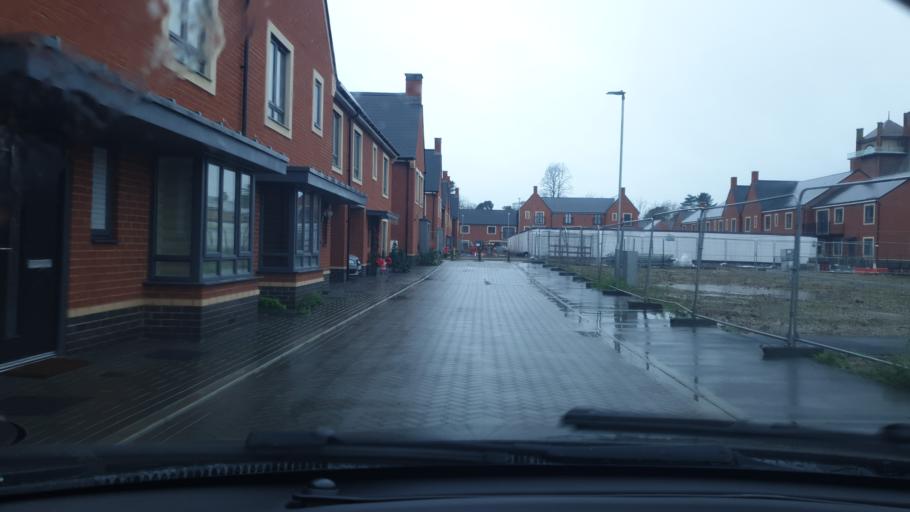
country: GB
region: England
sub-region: Essex
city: Colchester
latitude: 51.9178
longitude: 0.8978
